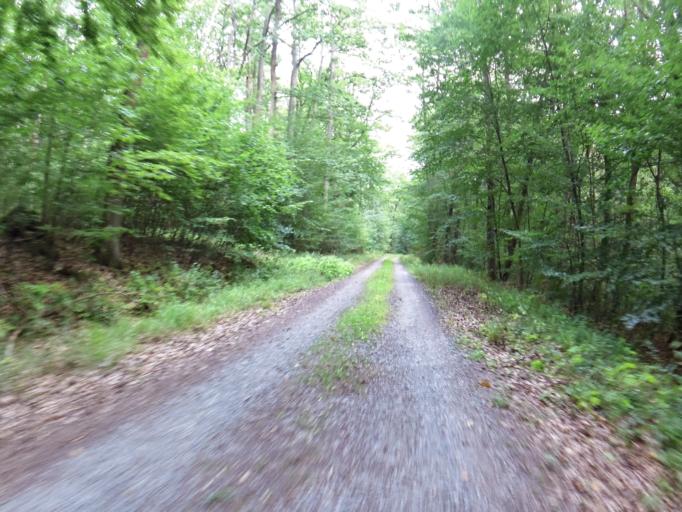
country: DE
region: Bavaria
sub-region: Regierungsbezirk Unterfranken
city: Margetshochheim
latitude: 49.8251
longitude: 9.8380
